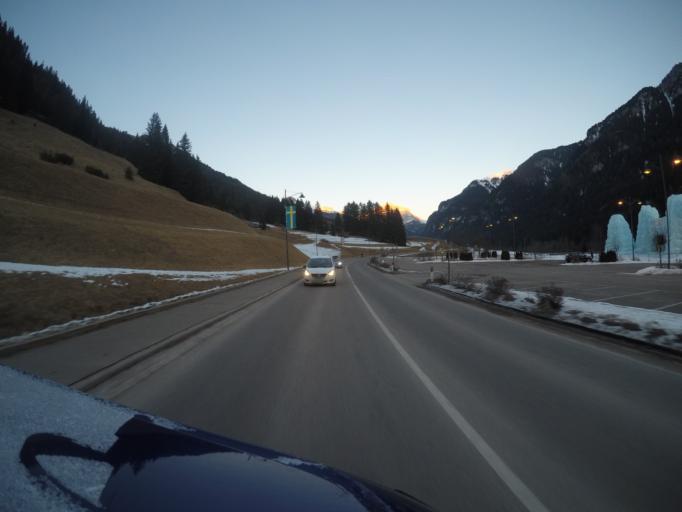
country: IT
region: Trentino-Alto Adige
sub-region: Provincia di Trento
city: Mazzin
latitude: 46.4589
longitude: 11.7019
